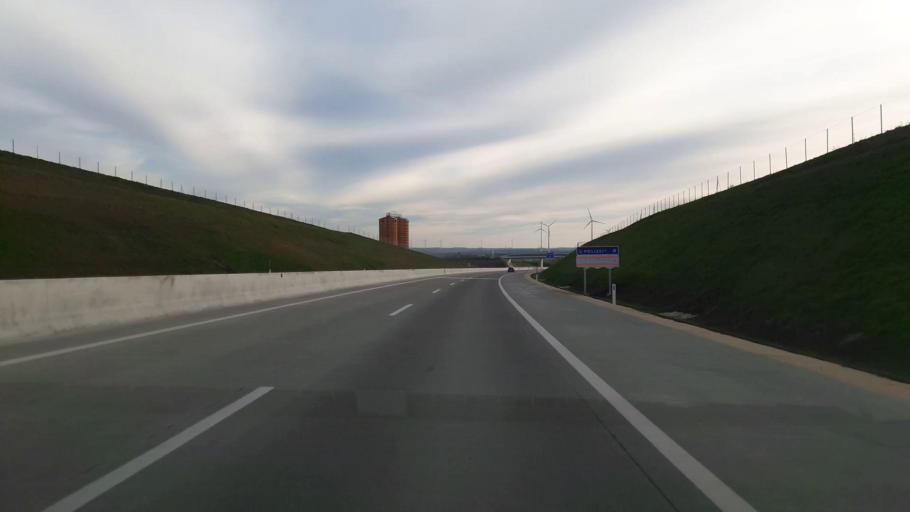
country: AT
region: Lower Austria
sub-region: Politischer Bezirk Mistelbach
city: Herrnbaumgarten
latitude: 48.6574
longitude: 16.6896
